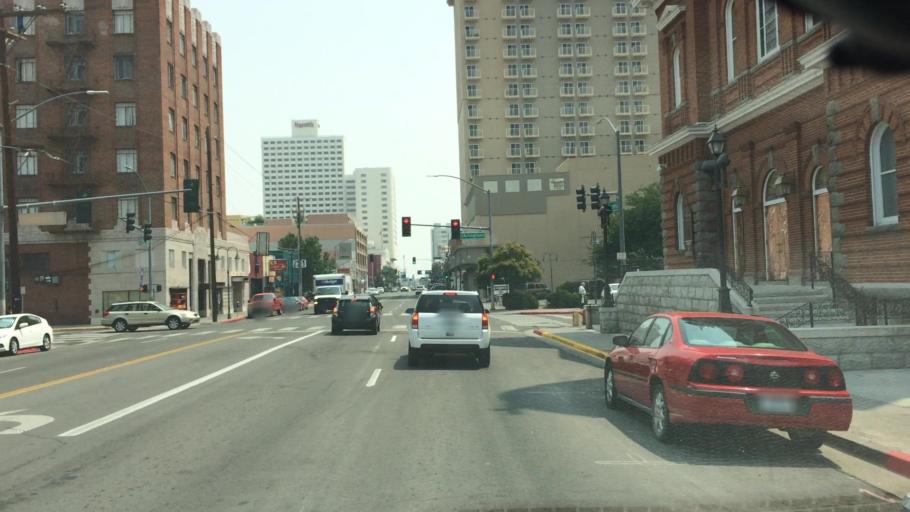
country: US
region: Nevada
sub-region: Washoe County
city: Reno
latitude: 39.5260
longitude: -119.8177
